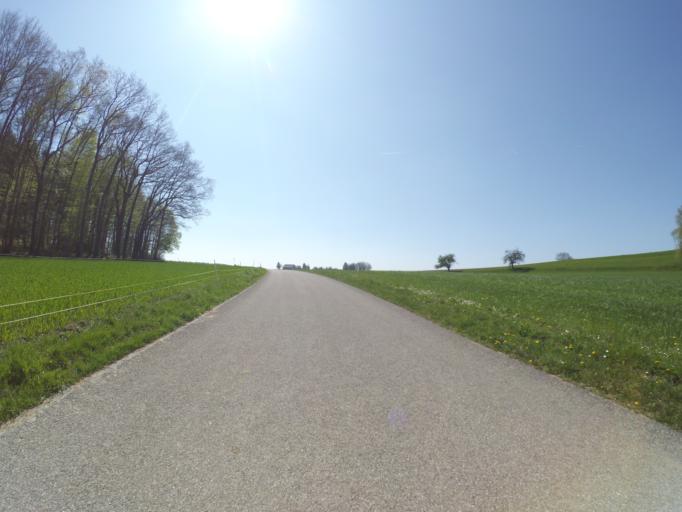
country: CH
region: Thurgau
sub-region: Frauenfeld District
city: Diessenhofen
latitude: 47.6314
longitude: 8.7373
